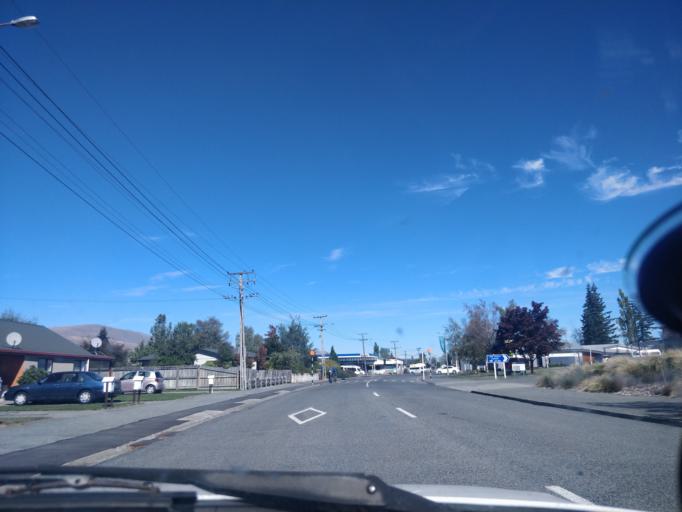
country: NZ
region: Canterbury
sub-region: Timaru District
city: Pleasant Point
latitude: -44.2565
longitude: 170.1009
